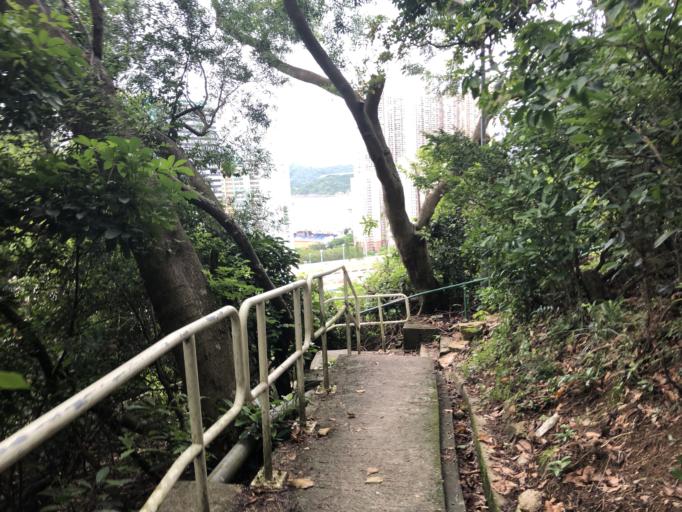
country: HK
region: Wanchai
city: Wan Chai
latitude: 22.2633
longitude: 114.2439
